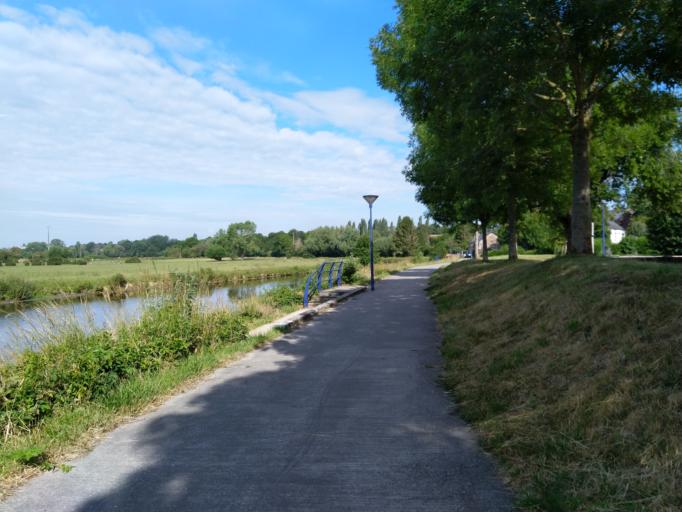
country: FR
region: Nord-Pas-de-Calais
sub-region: Departement du Nord
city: Rousies
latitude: 50.2842
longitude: 4.0145
